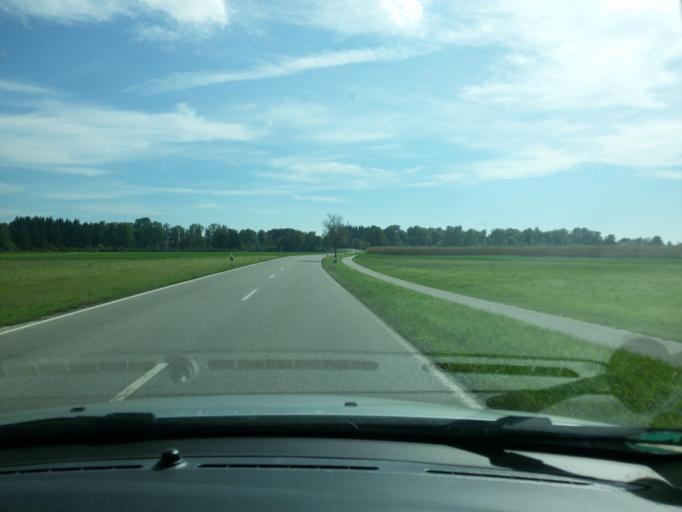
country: DE
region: Bavaria
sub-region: Swabia
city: Wehringen
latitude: 48.2595
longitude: 10.7871
